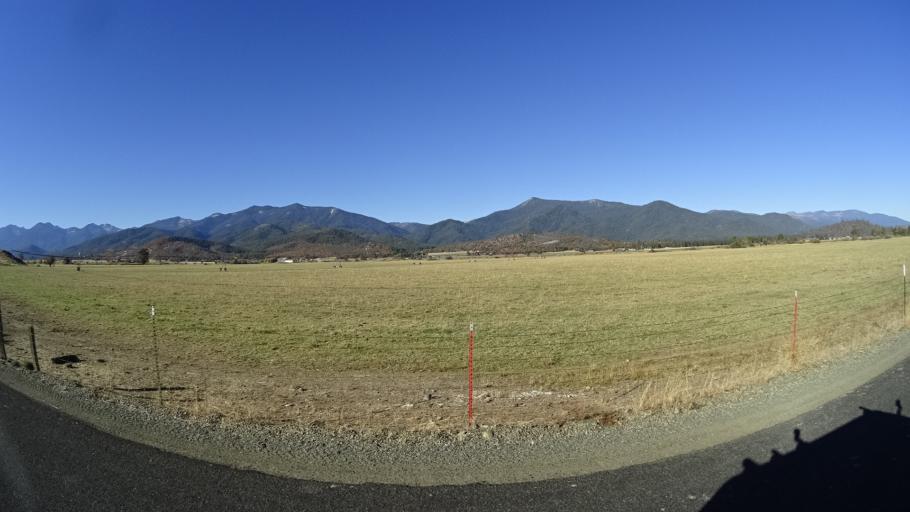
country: US
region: California
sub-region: Siskiyou County
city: Yreka
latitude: 41.4475
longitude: -122.8462
